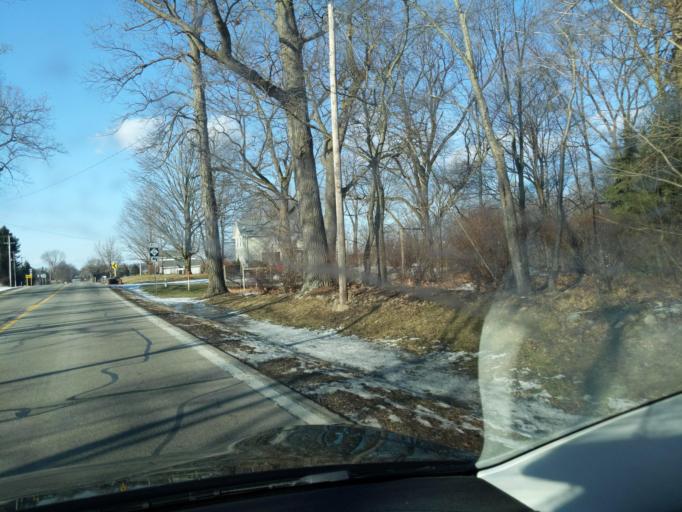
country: US
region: Michigan
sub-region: Ingham County
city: Stockbridge
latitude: 42.4808
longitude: -84.0859
